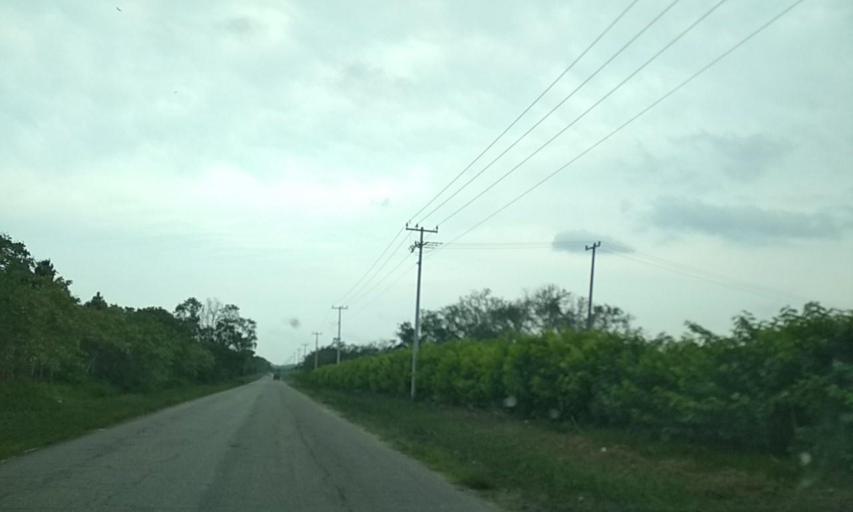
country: MX
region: Veracruz
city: Las Choapas
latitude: 17.8312
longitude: -94.1057
